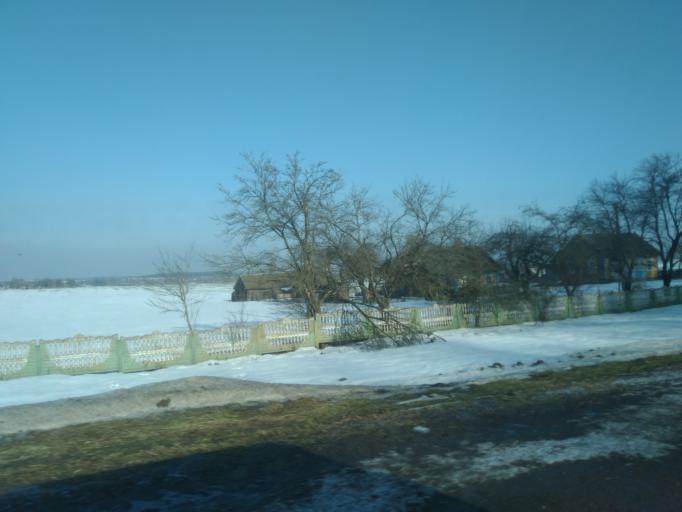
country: BY
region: Minsk
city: Snow
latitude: 53.2141
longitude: 26.4501
